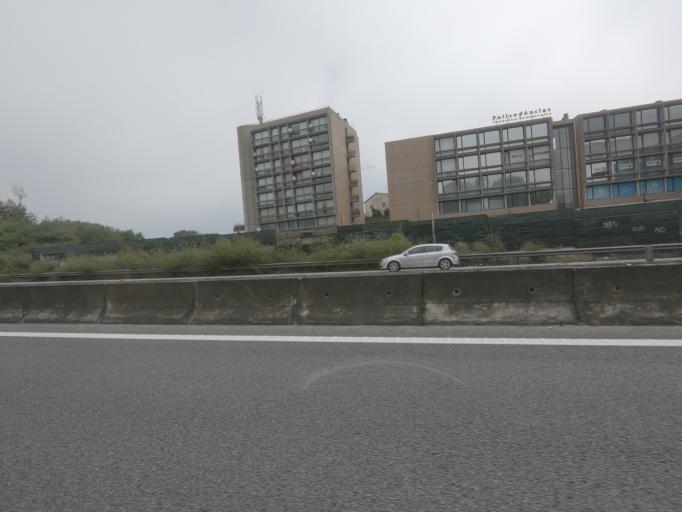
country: PT
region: Porto
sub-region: Matosinhos
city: Leca da Palmeira
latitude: 41.2001
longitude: -8.6880
